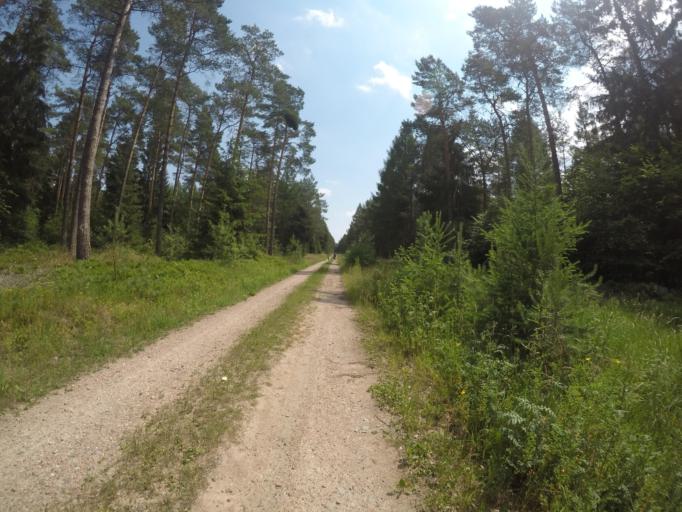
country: DE
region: Lower Saxony
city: Asendorf
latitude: 53.2551
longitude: 9.9413
